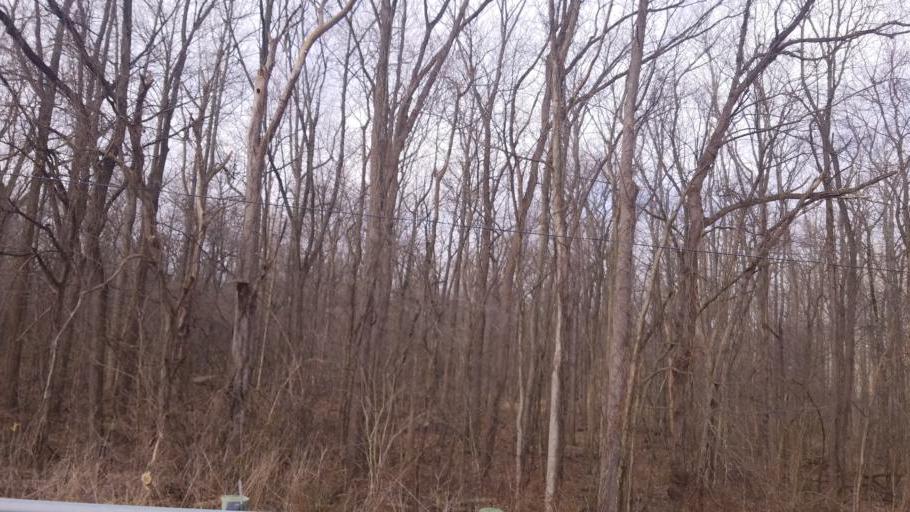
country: US
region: Ohio
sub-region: Crawford County
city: Bucyrus
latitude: 40.7482
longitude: -82.9058
